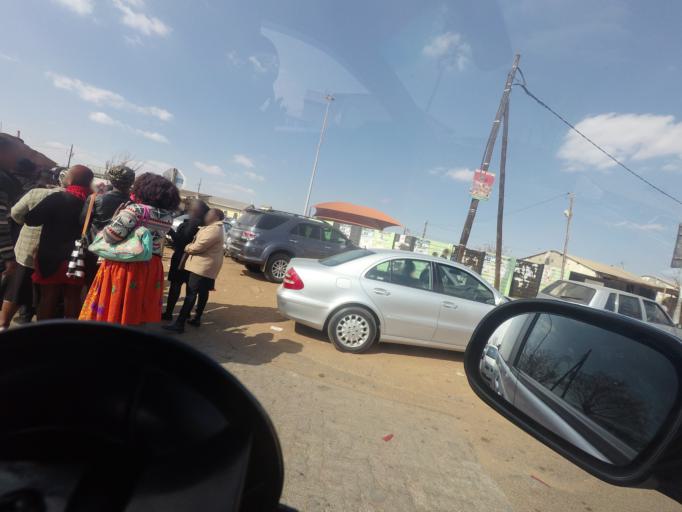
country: ZA
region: Gauteng
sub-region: Sedibeng District Municipality
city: Heidelberg
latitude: -26.5508
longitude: 28.3300
